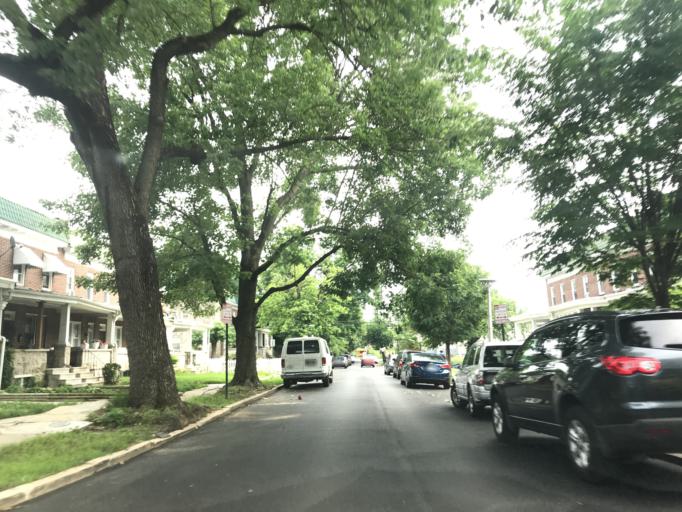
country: US
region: Maryland
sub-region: City of Baltimore
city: Baltimore
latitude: 39.3109
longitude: -76.6613
